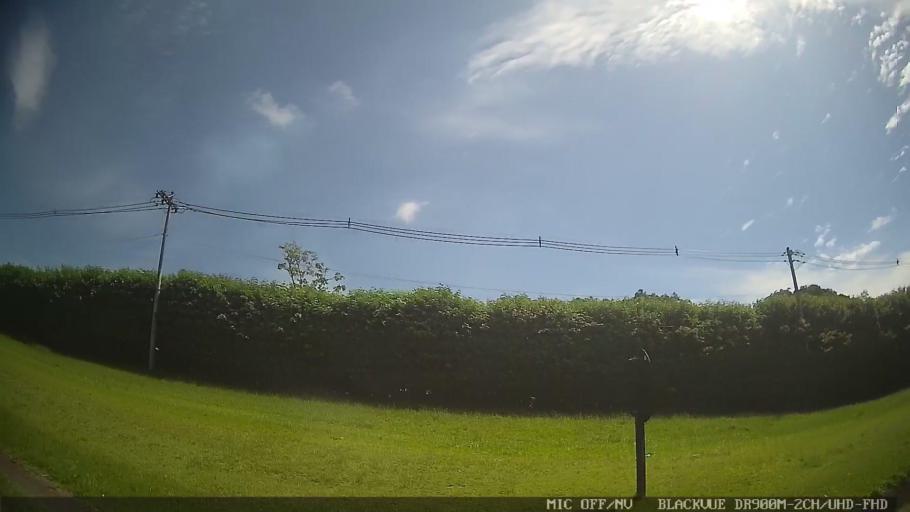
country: BR
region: Sao Paulo
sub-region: Porto Feliz
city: Porto Feliz
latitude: -23.2127
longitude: -47.5755
